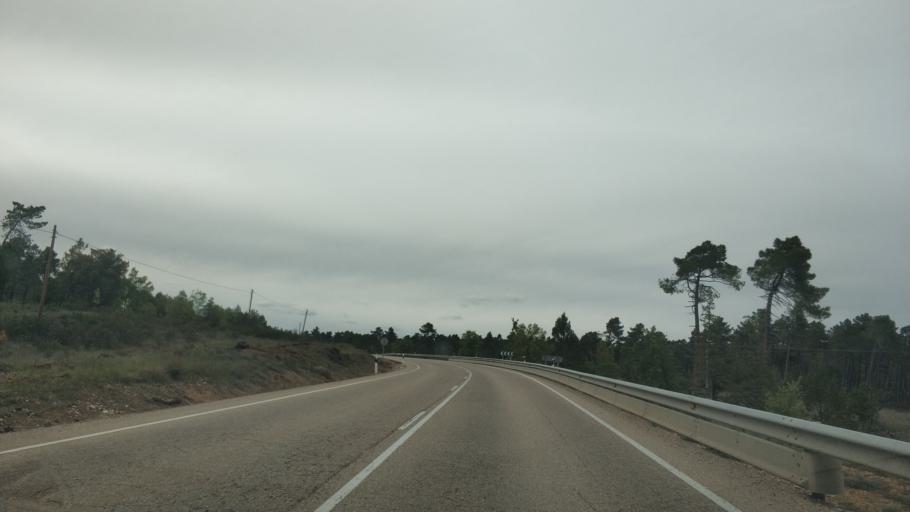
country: ES
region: Castille and Leon
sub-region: Provincia de Soria
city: Bayubas de Abajo
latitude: 41.5180
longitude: -2.9296
